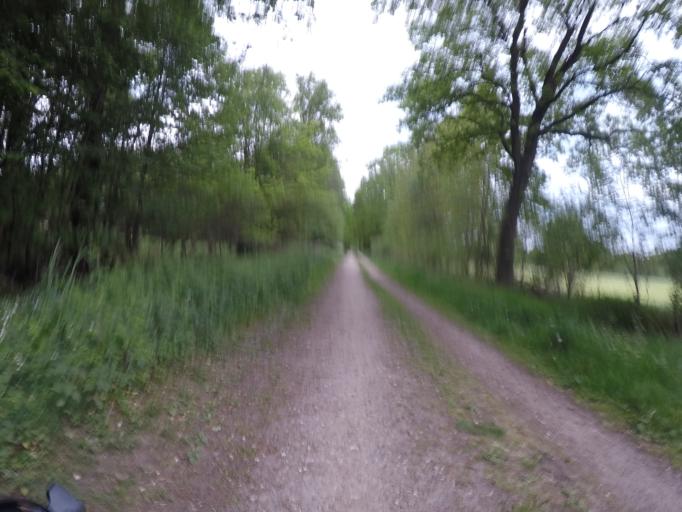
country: DE
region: Schleswig-Holstein
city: Henstedt-Ulzburg
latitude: 53.7635
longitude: 10.0151
